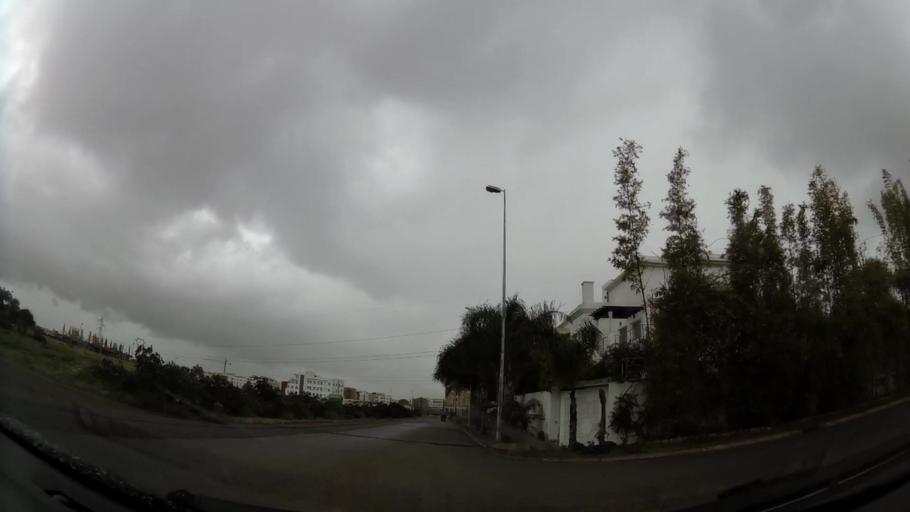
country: MA
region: Grand Casablanca
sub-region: Casablanca
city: Casablanca
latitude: 33.5333
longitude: -7.6193
